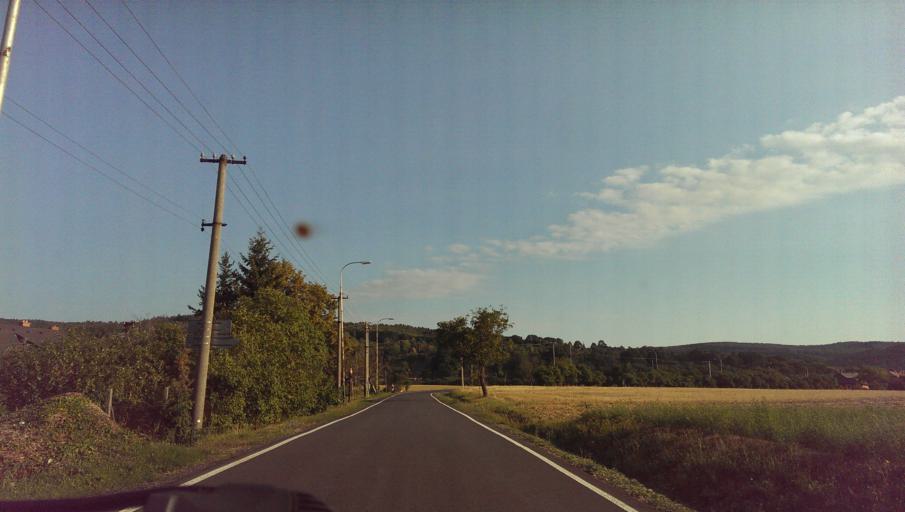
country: CZ
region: South Moravian
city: Zeravice
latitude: 49.0597
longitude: 17.2191
